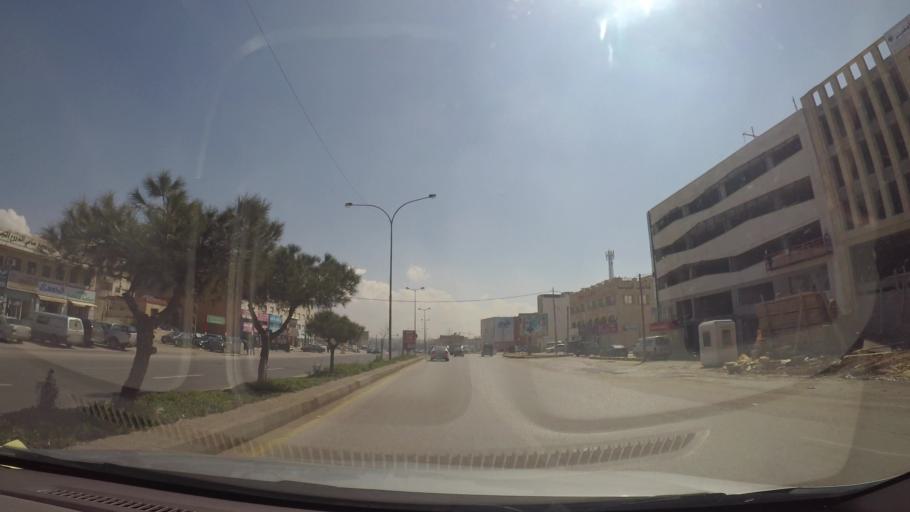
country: JO
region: Amman
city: Al Bunayyat ash Shamaliyah
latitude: 31.9002
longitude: 35.8943
